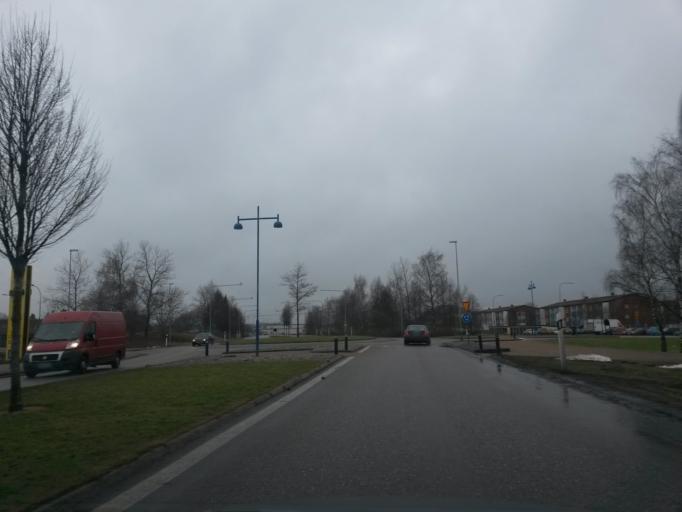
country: SE
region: Vaestra Goetaland
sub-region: Vanersborgs Kommun
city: Vanersborg
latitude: 58.3650
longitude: 12.3422
